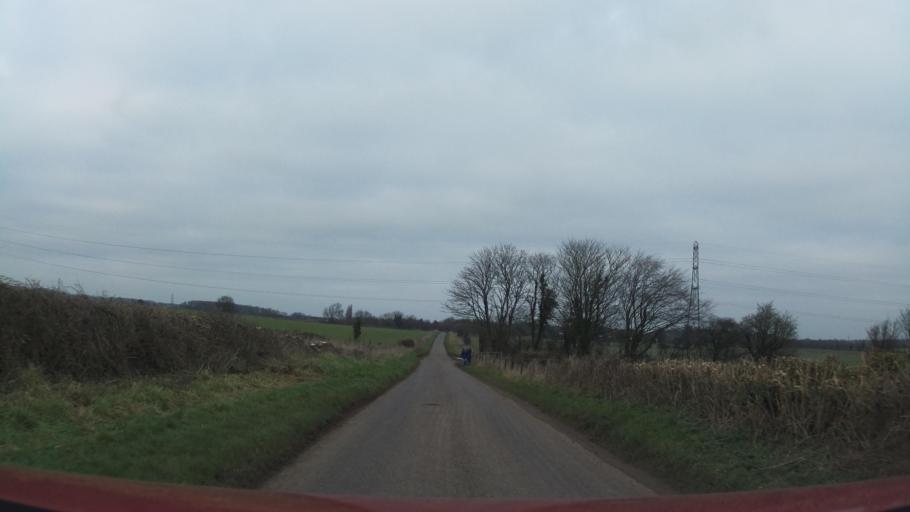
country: GB
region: England
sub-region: Wiltshire
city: Nettleton
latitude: 51.4860
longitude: -2.2817
